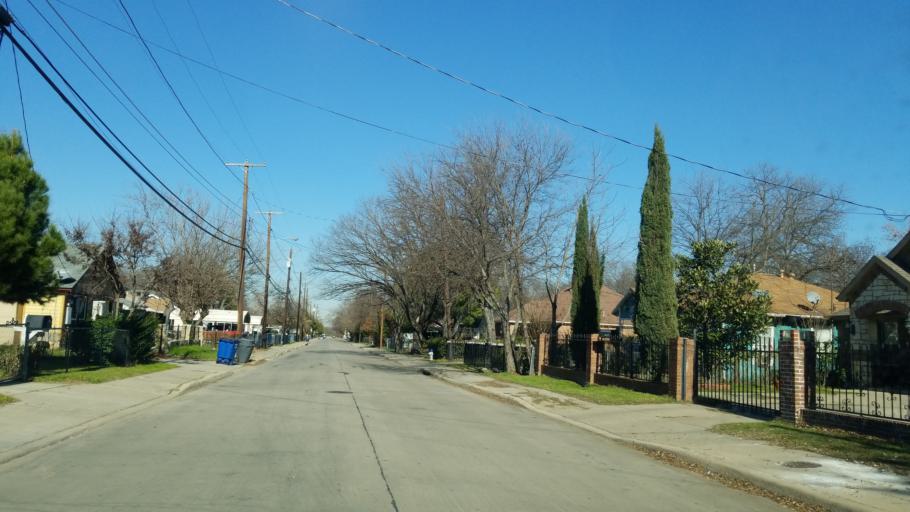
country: US
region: Texas
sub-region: Dallas County
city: Cockrell Hill
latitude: 32.7537
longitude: -96.9115
